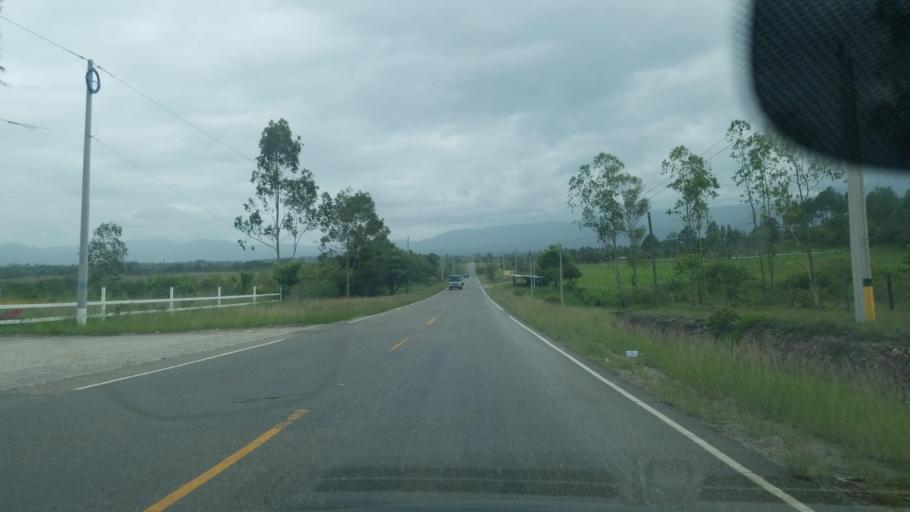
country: HN
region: Ocotepeque
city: Lucerna
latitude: 14.5396
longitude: -88.9465
